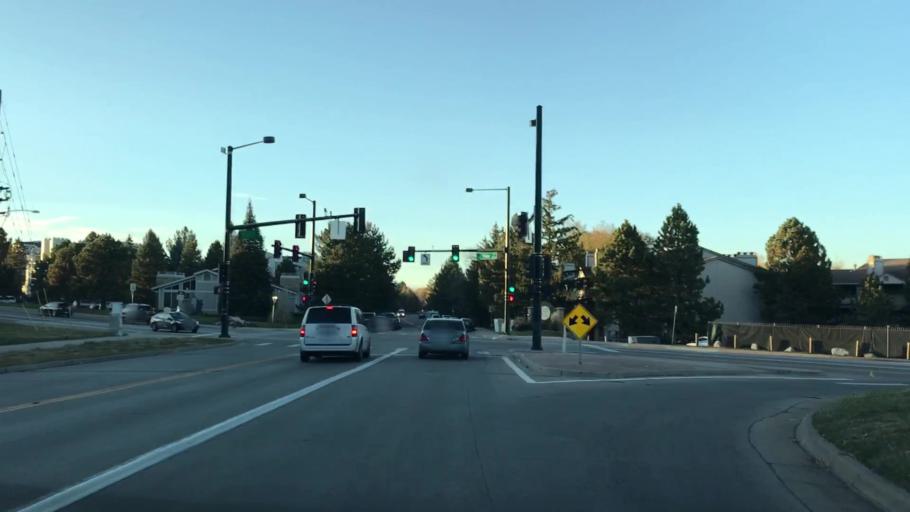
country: US
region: Colorado
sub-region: Arapahoe County
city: Glendale
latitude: 39.6673
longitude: -104.8937
